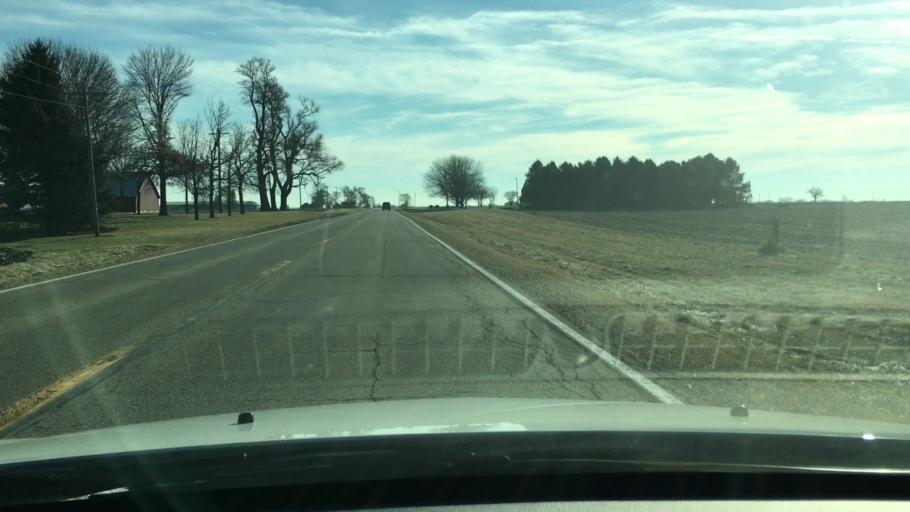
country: US
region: Illinois
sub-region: LaSalle County
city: Mendota
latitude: 41.4755
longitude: -89.1266
